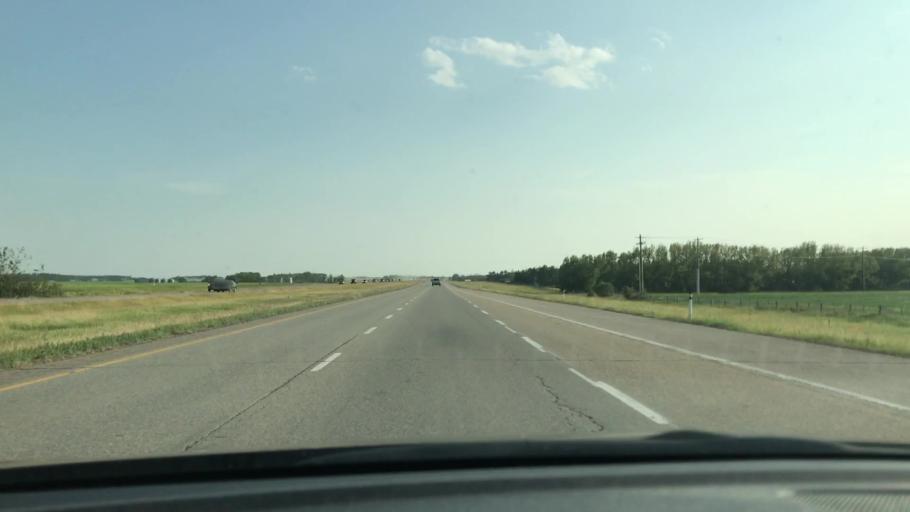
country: CA
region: Alberta
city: Leduc
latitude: 53.2229
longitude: -113.5789
